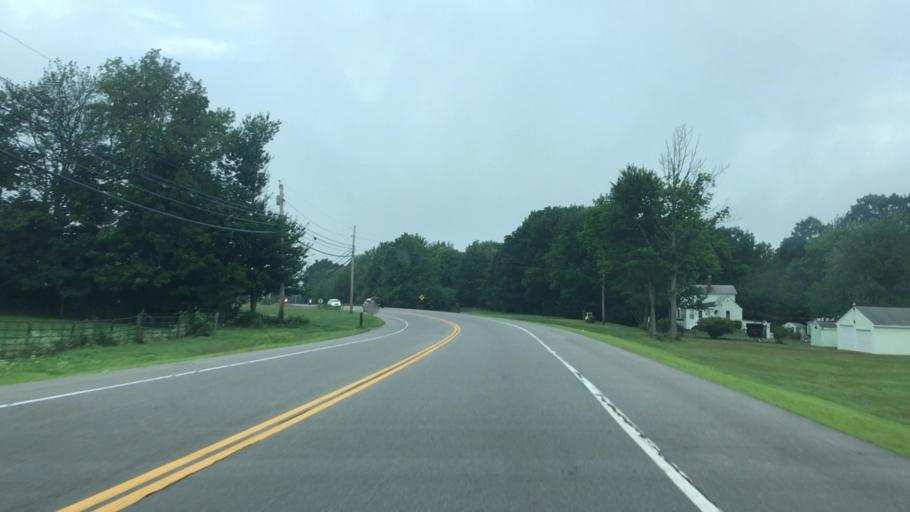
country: US
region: Maine
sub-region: York County
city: Lebanon
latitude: 43.4226
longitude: -70.8202
